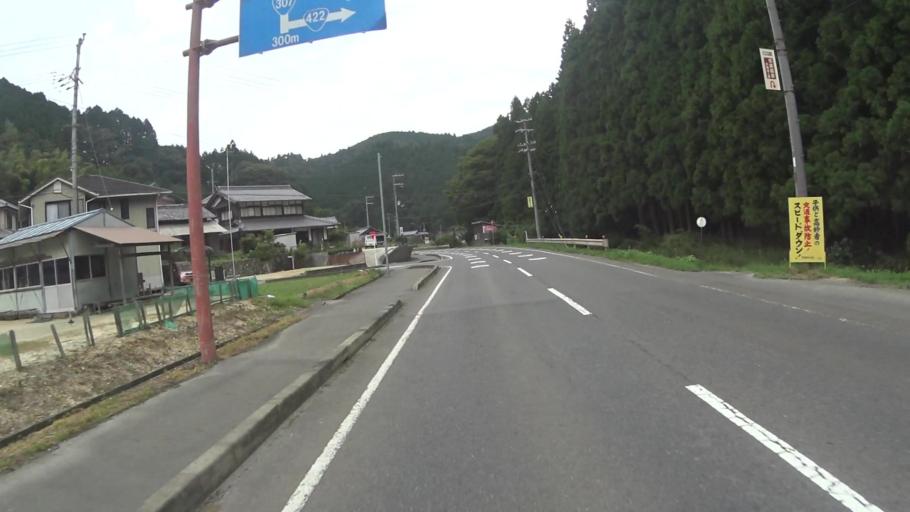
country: JP
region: Shiga Prefecture
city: Kusatsu
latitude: 34.8595
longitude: 135.9715
